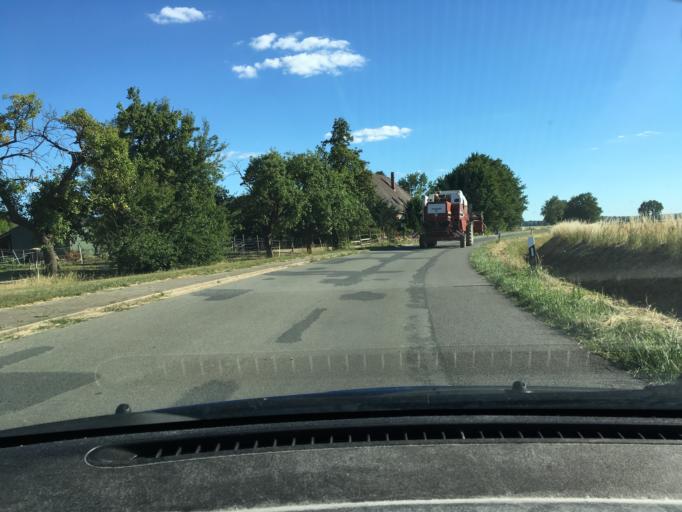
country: DE
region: Mecklenburg-Vorpommern
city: Boizenburg
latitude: 53.3450
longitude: 10.7240
